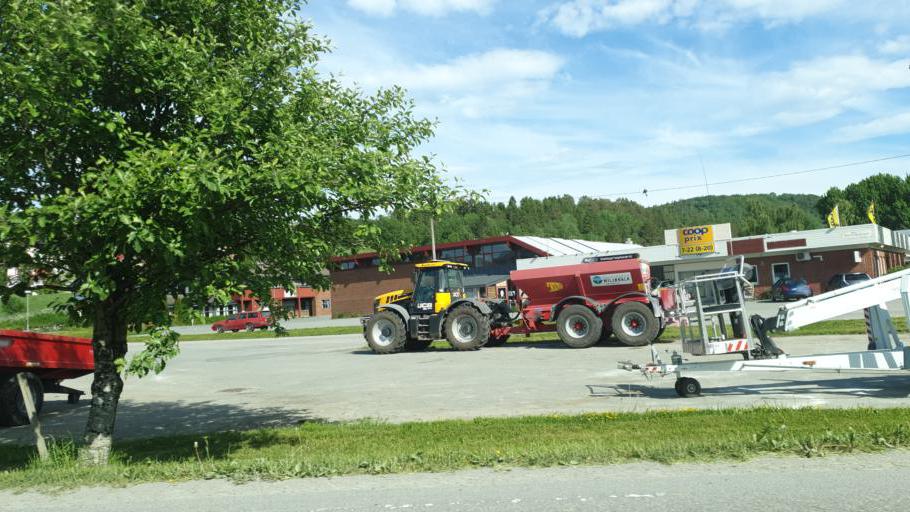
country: NO
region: Sor-Trondelag
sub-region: Rissa
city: Rissa
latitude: 63.5089
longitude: 10.0180
